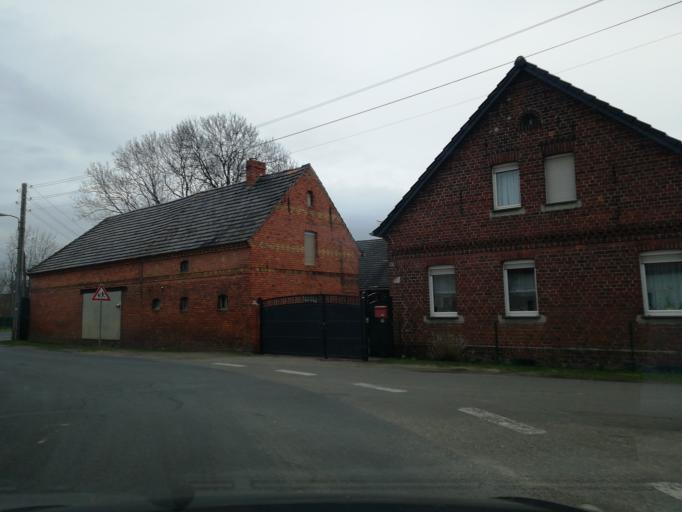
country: DE
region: Brandenburg
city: Calau
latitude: 51.7306
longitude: 14.0153
